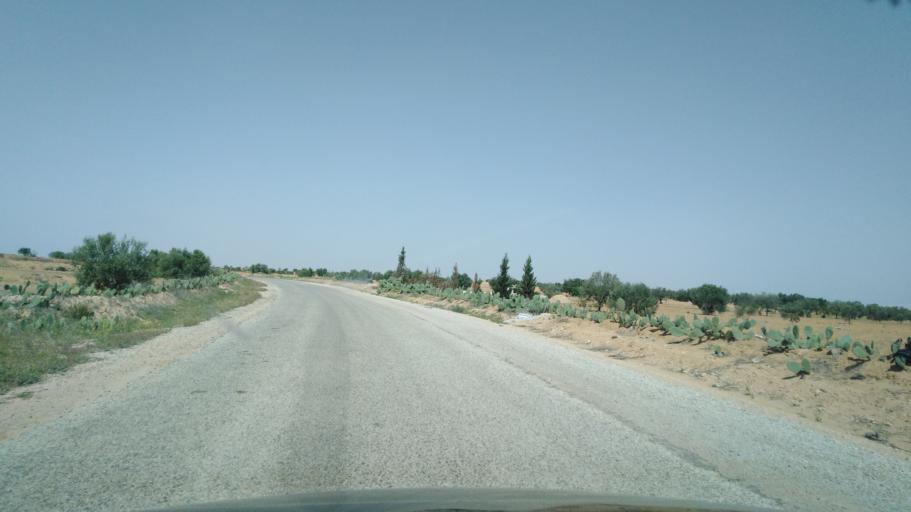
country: TN
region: Safaqis
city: Bi'r `Ali Bin Khalifah
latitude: 34.6789
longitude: 10.4122
